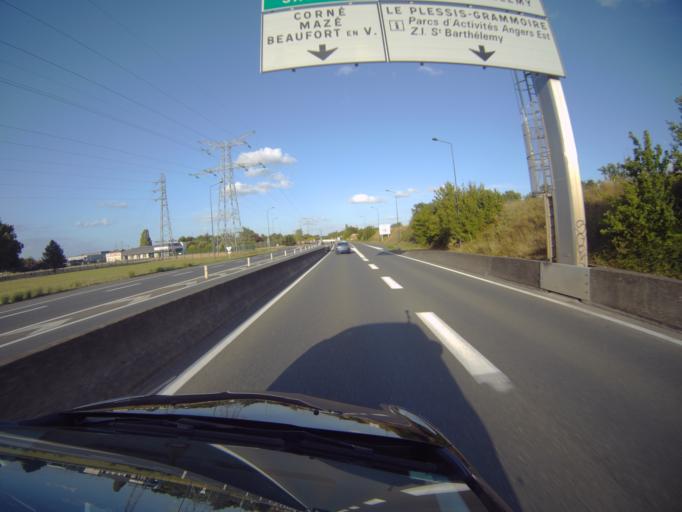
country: FR
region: Pays de la Loire
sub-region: Departement de Maine-et-Loire
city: Trelaze
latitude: 47.4724
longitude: -0.4971
